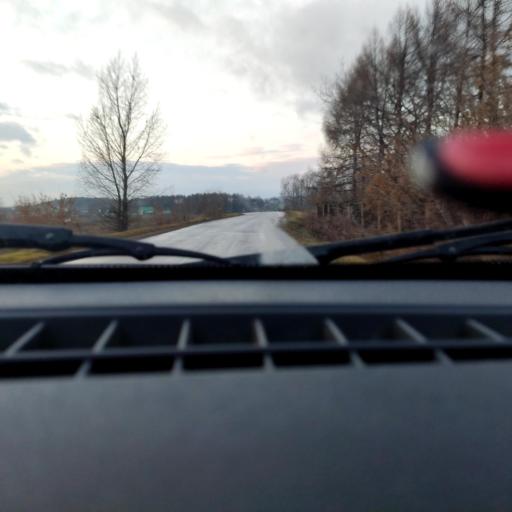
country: RU
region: Bashkortostan
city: Avdon
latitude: 54.5107
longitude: 55.8245
